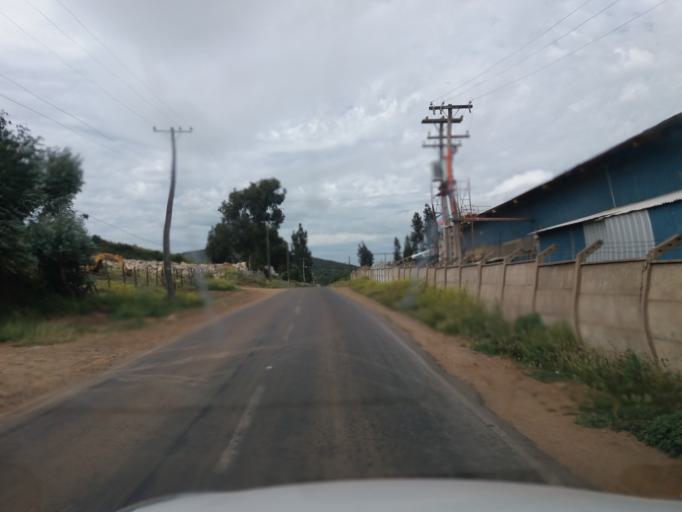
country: CL
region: Valparaiso
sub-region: Provincia de Marga Marga
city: Quilpue
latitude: -32.9177
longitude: -71.4352
